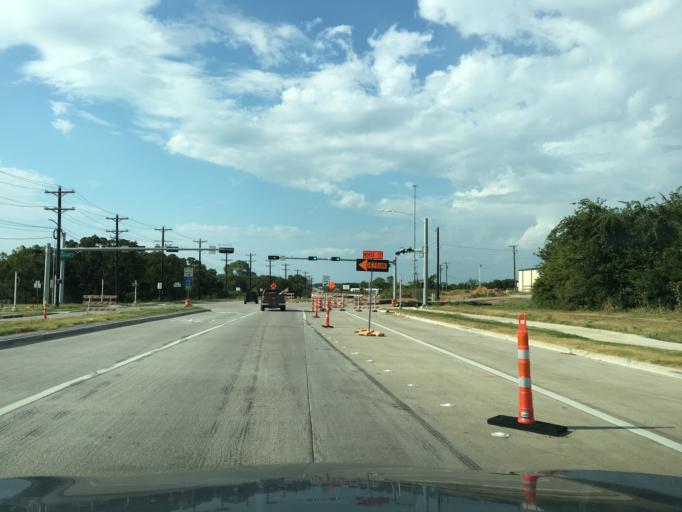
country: US
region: Texas
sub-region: Denton County
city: Corinth
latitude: 33.1944
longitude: -97.0853
